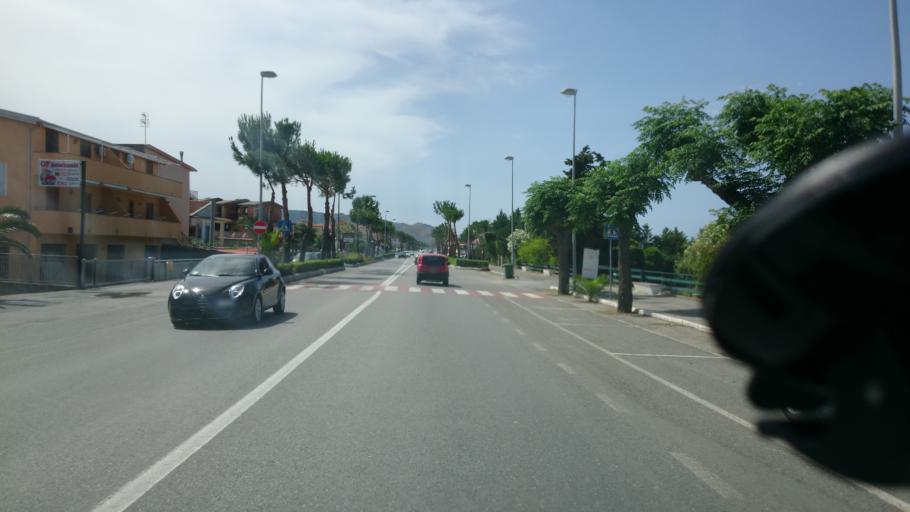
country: IT
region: Calabria
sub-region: Provincia di Cosenza
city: Marcellina
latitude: 39.7554
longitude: 15.8039
